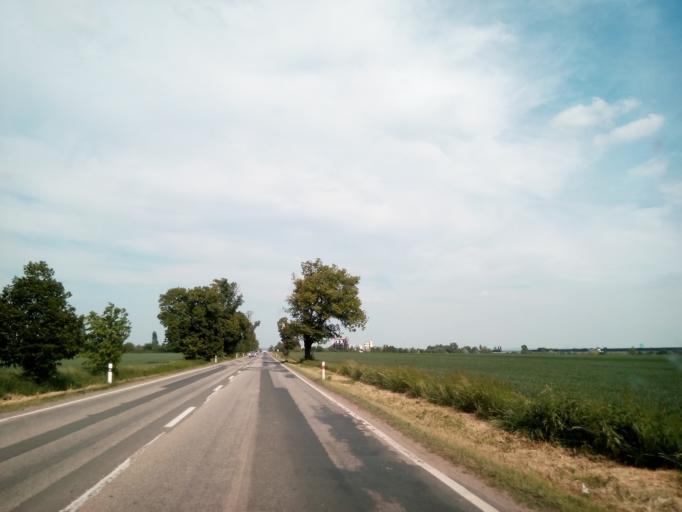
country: CZ
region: South Moravian
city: Blazovice
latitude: 49.1847
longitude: 16.7936
